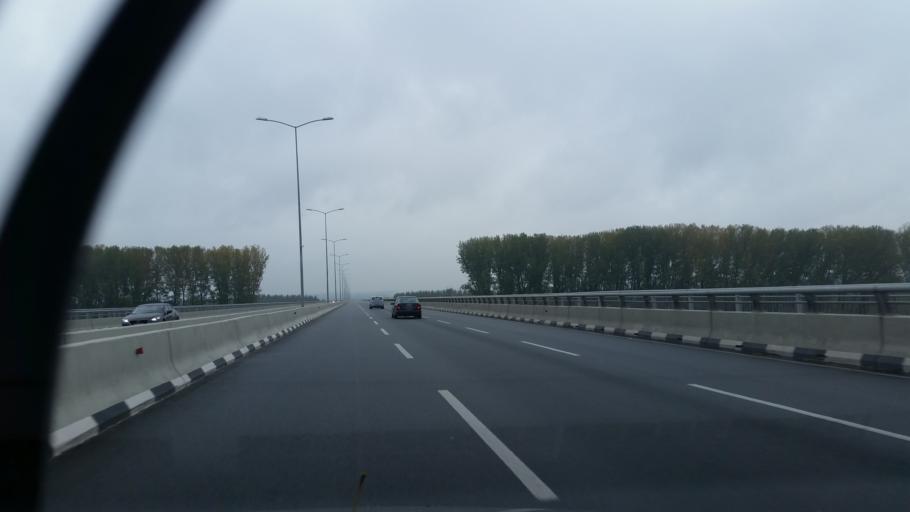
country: RS
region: Central Serbia
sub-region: Belgrade
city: Zemun
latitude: 44.8654
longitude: 20.3818
